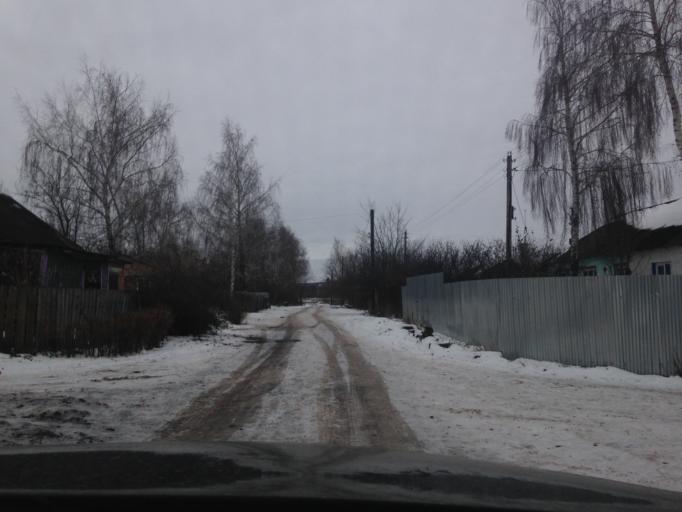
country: RU
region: Tula
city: Priupskiy
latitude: 53.7778
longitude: 37.6527
